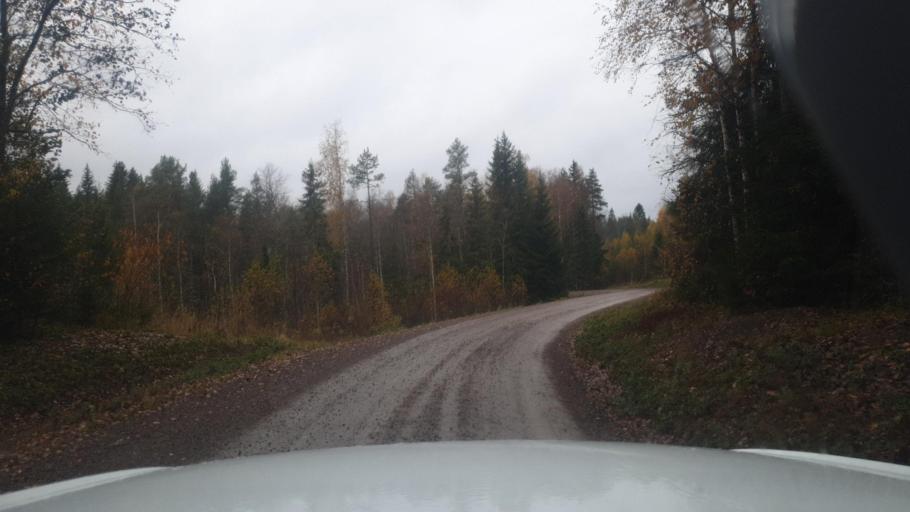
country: SE
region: Vaermland
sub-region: Eda Kommun
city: Charlottenberg
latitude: 60.0899
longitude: 12.5048
